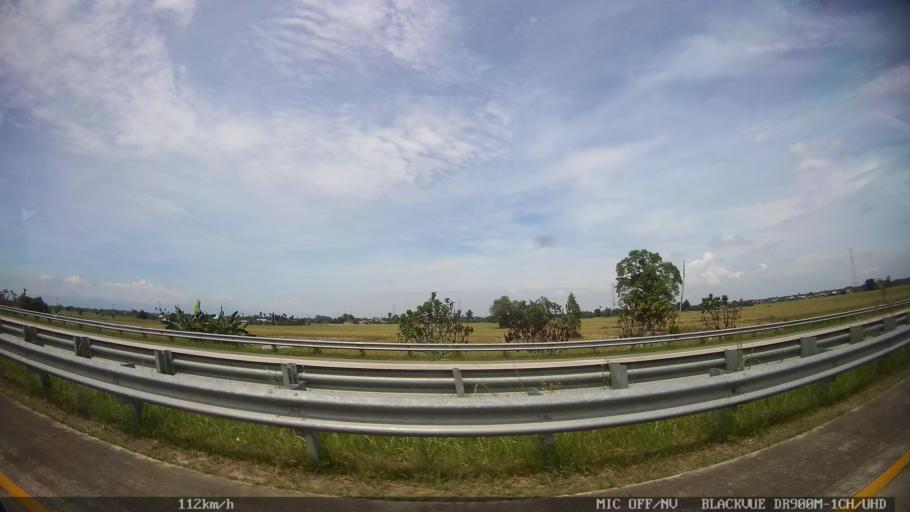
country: ID
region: North Sumatra
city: Percut
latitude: 3.5756
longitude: 98.8469
